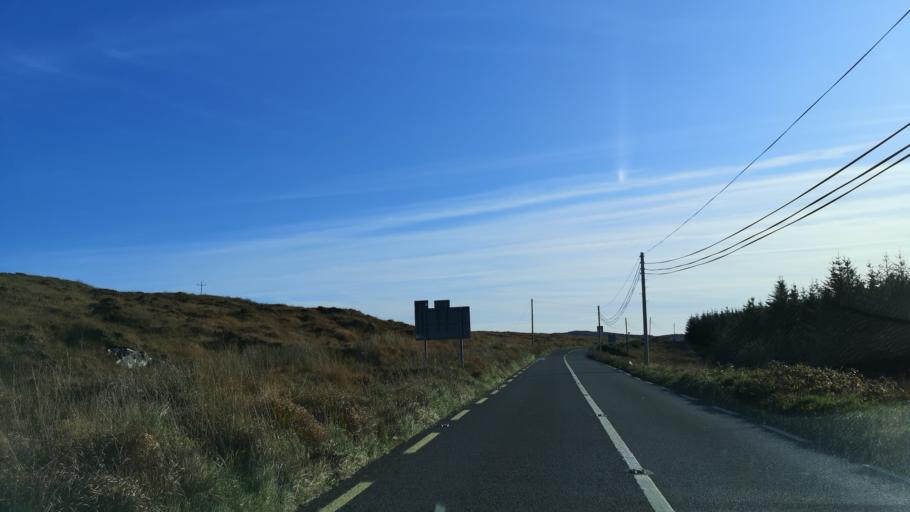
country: IE
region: Connaught
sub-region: County Galway
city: Clifden
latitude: 53.5264
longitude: -10.0479
